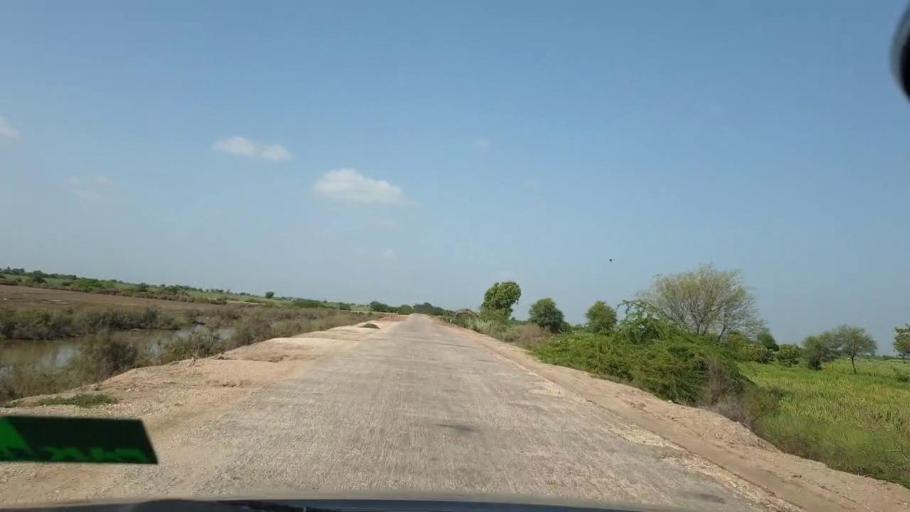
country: PK
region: Sindh
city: Tando Bago
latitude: 24.6925
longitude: 69.1892
